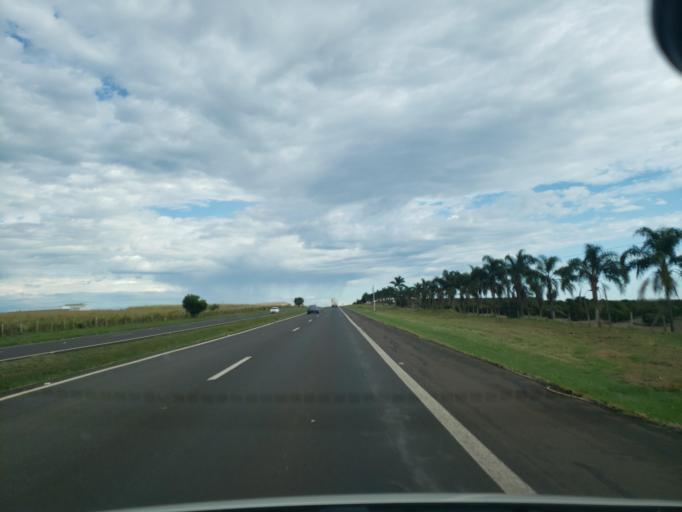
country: BR
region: Sao Paulo
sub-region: Jau
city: Jau
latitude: -22.2672
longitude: -48.5026
